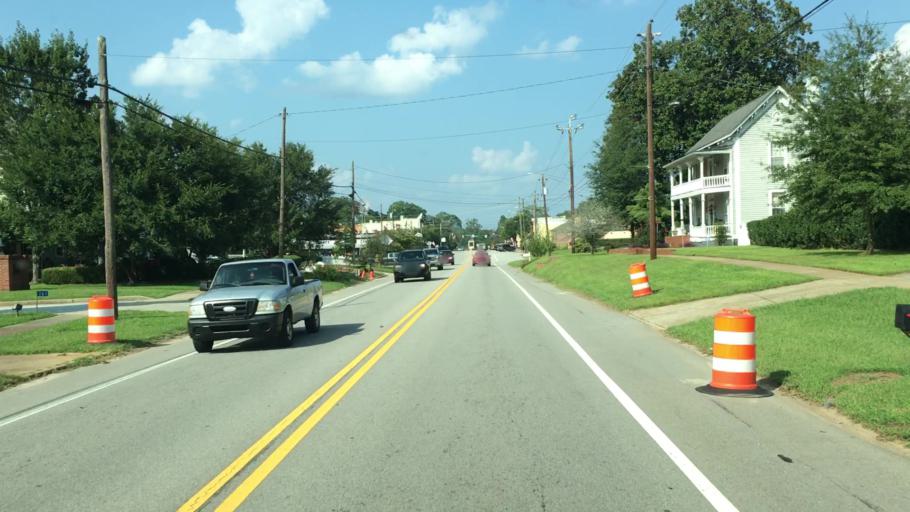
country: US
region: Georgia
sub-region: Walton County
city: Social Circle
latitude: 33.6538
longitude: -83.7205
